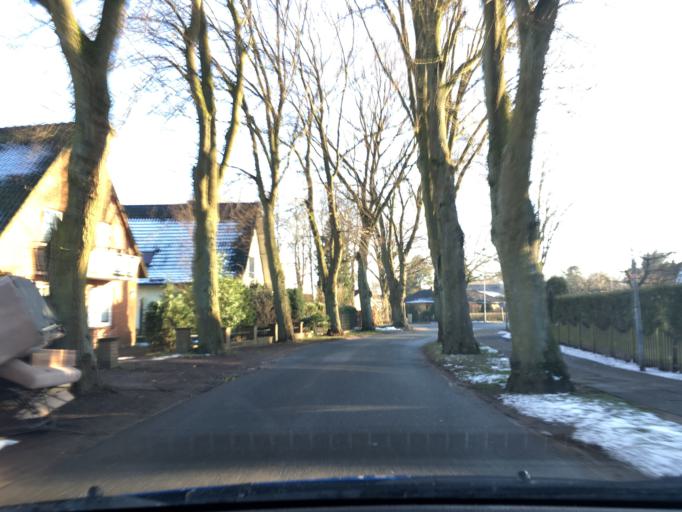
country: DE
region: Schleswig-Holstein
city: Buchen
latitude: 53.4827
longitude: 10.6071
